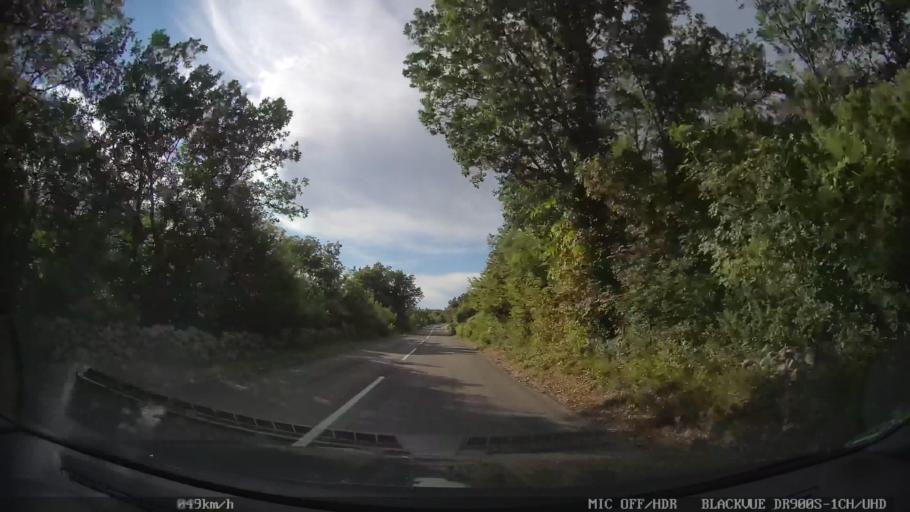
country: HR
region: Primorsko-Goranska
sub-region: Grad Krk
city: Krk
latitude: 45.0592
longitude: 14.4831
